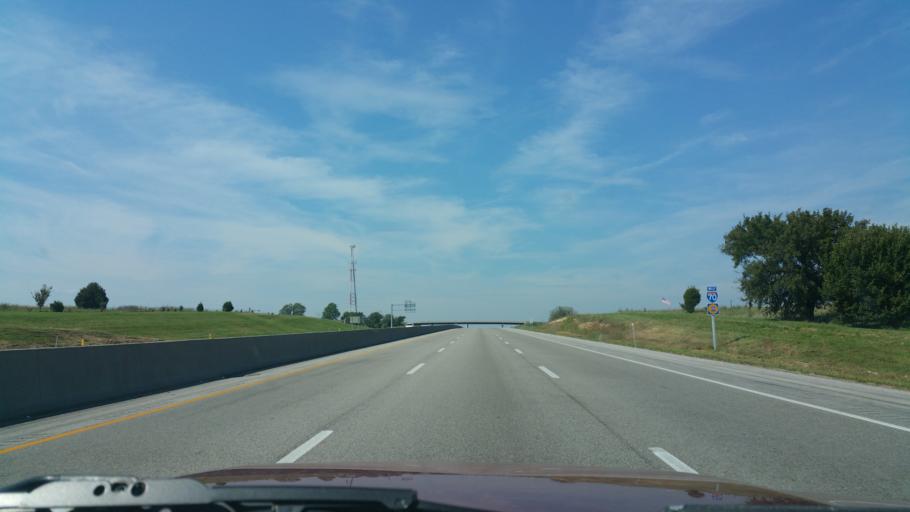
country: US
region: Kansas
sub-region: Douglas County
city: Lawrence
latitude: 38.9971
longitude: -95.3478
